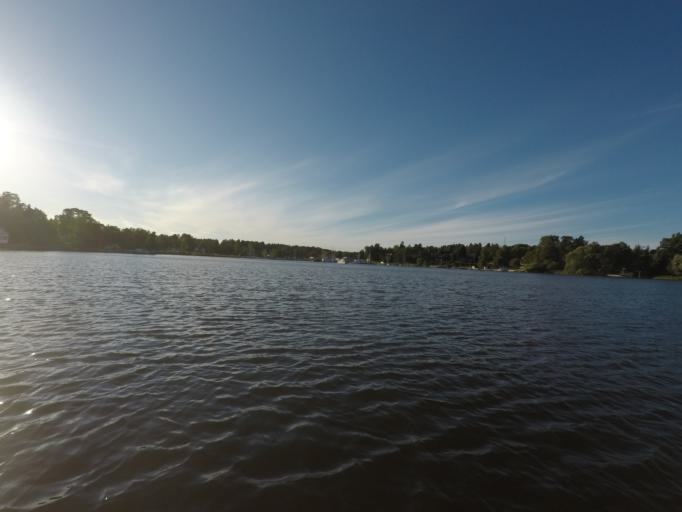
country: SE
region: Soedermanland
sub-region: Eskilstuna Kommun
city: Kvicksund
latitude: 59.4577
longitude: 16.3222
